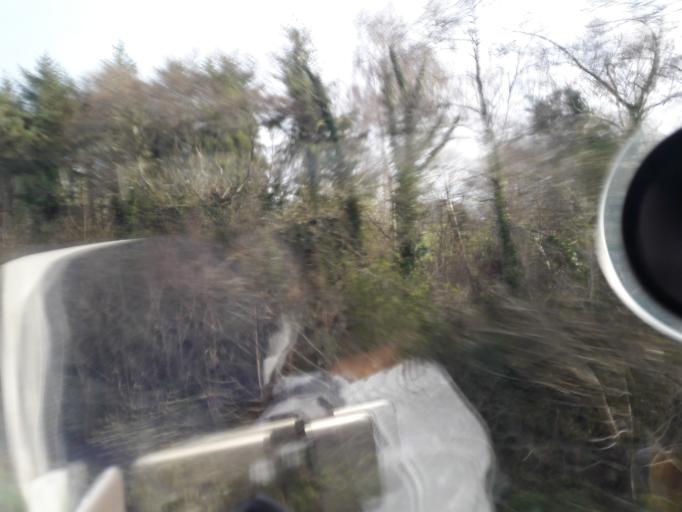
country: IE
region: Leinster
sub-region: An Iarmhi
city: Kinnegad
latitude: 53.4749
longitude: -7.0301
